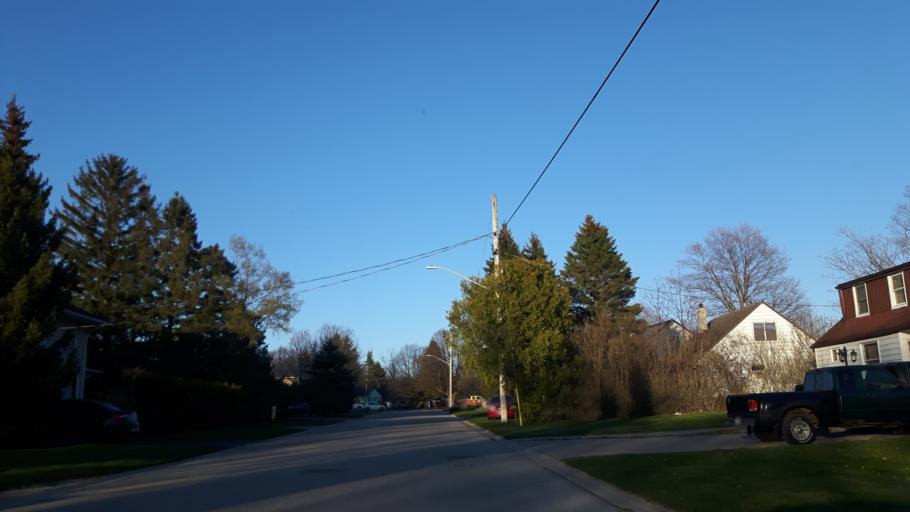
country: CA
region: Ontario
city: Bluewater
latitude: 43.5818
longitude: -81.5191
